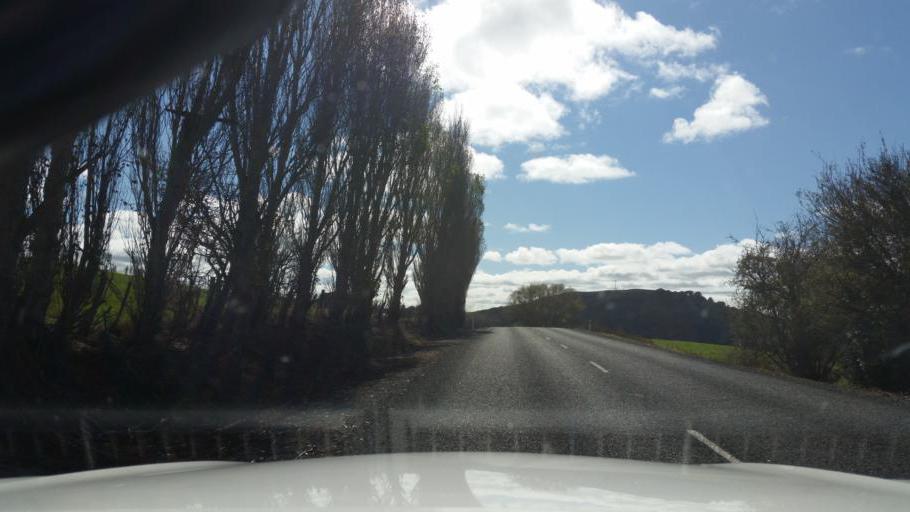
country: NZ
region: Northland
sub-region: Kaipara District
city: Dargaville
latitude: -36.1684
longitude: 174.1659
